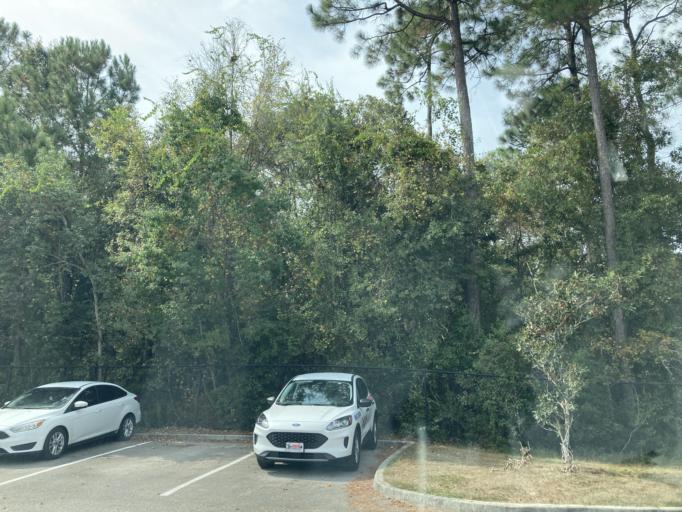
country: US
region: Mississippi
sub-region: Jackson County
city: Gulf Hills
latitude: 30.4523
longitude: -88.8454
